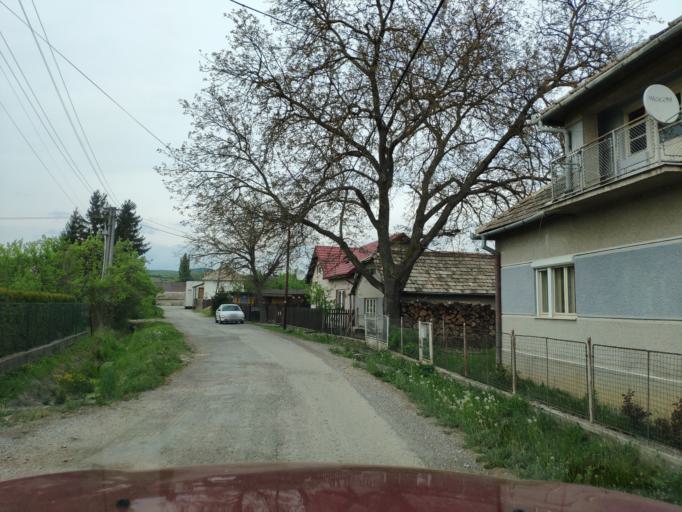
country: SK
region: Banskobystricky
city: Rimavska Sobota
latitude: 48.4836
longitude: 20.0915
